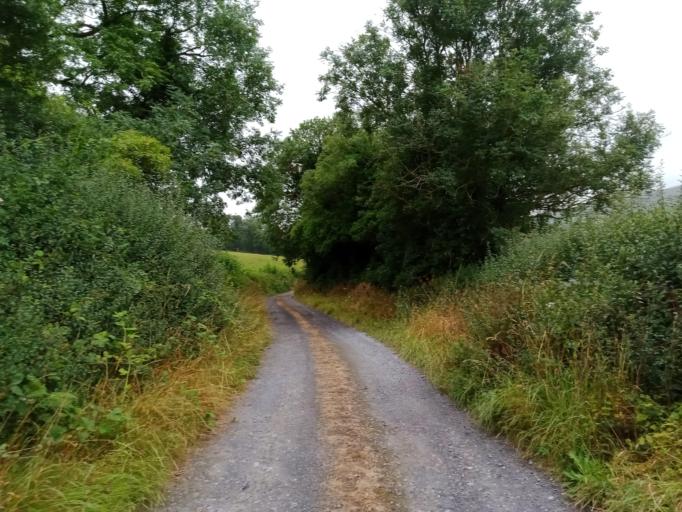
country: IE
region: Leinster
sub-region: Kilkenny
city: Ballyragget
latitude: 52.8121
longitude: -7.4315
